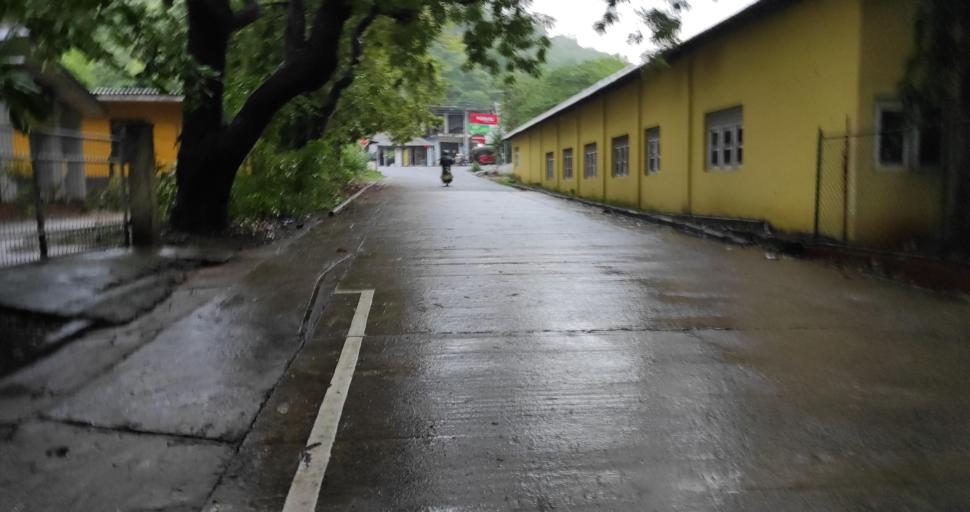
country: LK
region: Eastern Province
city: Trincomalee
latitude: 8.3663
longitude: 81.0036
